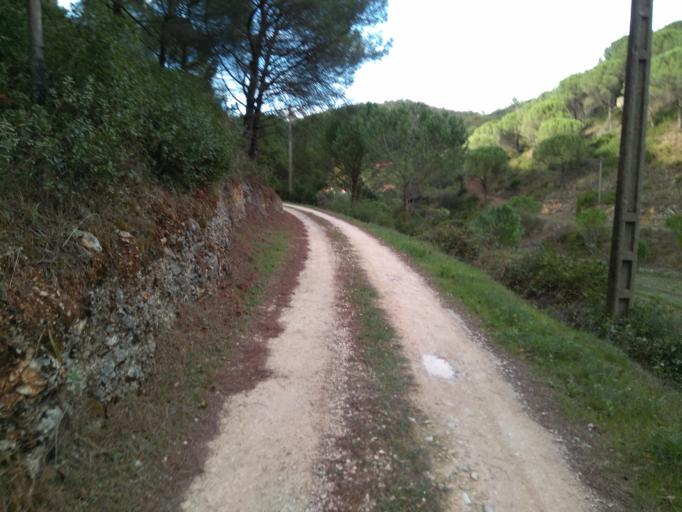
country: PT
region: Leiria
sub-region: Porto de Mos
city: Porto de Mos
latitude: 39.5920
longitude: -8.8097
